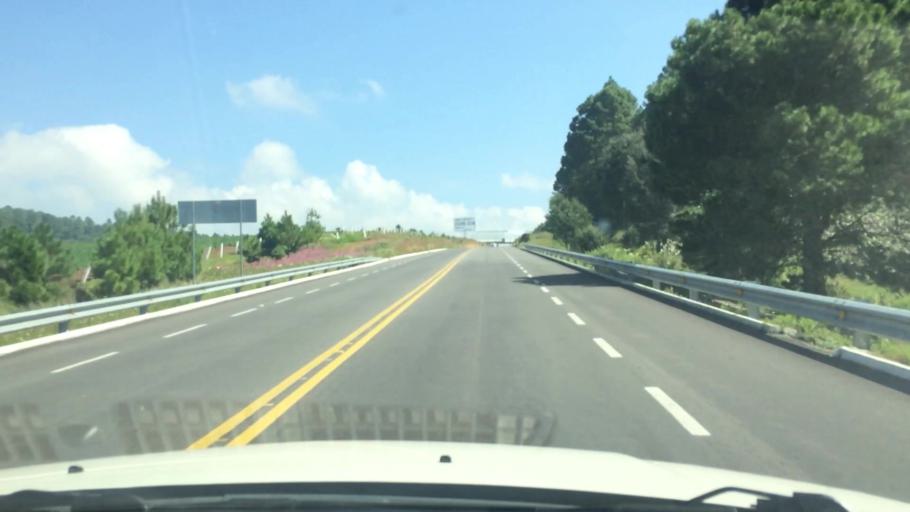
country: MX
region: Mexico
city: Amanalco de Becerra
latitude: 19.3015
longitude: -100.0109
